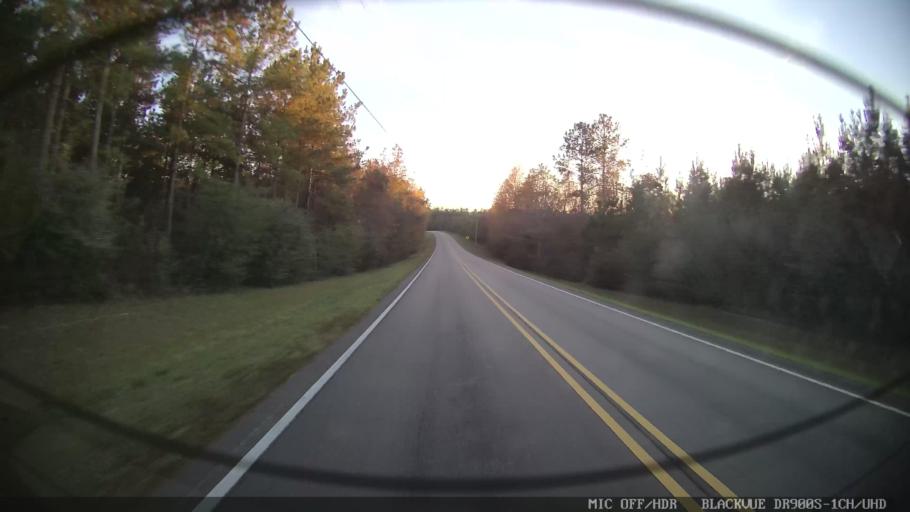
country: US
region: Mississippi
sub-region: Lamar County
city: Purvis
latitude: 31.0205
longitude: -89.2531
